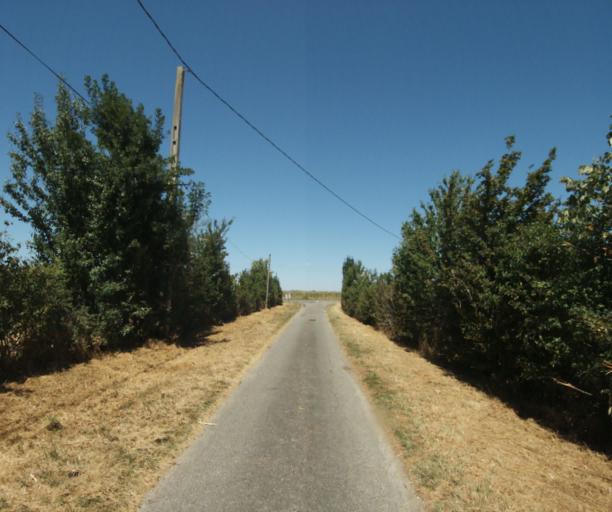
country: FR
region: Midi-Pyrenees
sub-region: Departement de la Haute-Garonne
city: Saint-Felix-Lauragais
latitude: 43.4727
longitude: 1.9417
